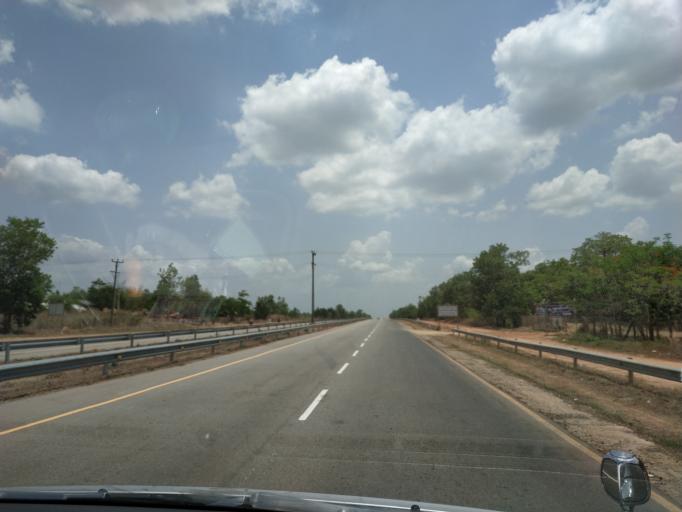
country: MM
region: Bago
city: Thanatpin
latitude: 17.3057
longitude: 96.2231
